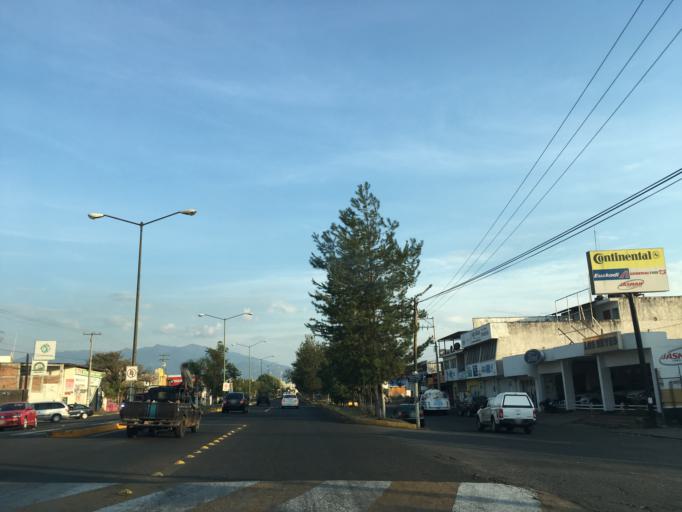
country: MX
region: Michoacan
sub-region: Los Reyes
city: La Higuerita (Colonia San Rafael)
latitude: 19.5983
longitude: -102.4747
